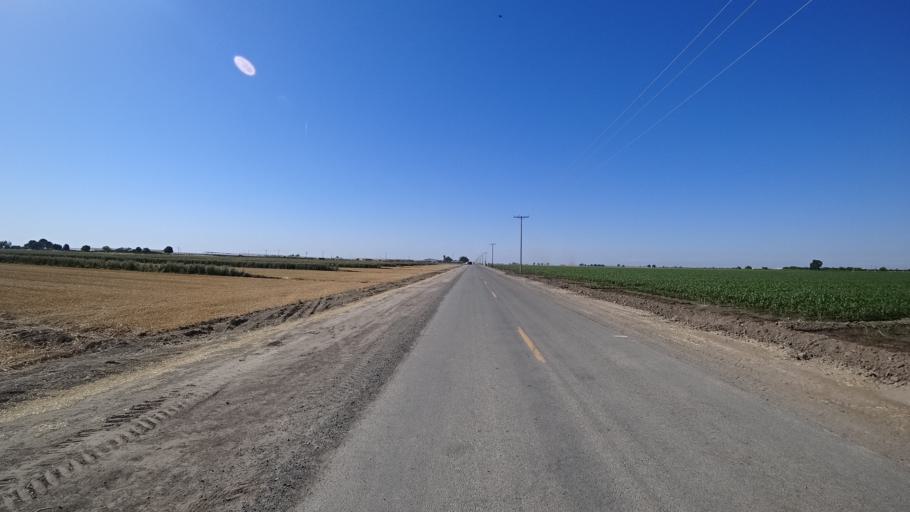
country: US
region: California
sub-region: Kings County
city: Home Garden
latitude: 36.2511
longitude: -119.5563
